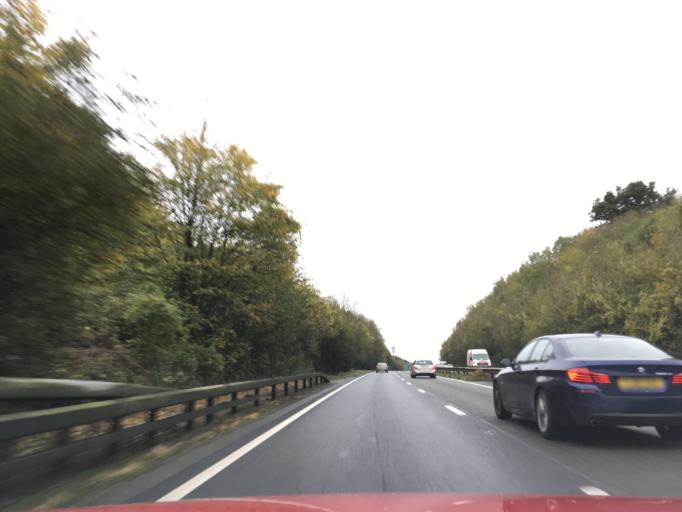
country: GB
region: England
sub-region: Hampshire
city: Overton
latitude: 51.1866
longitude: -1.3363
